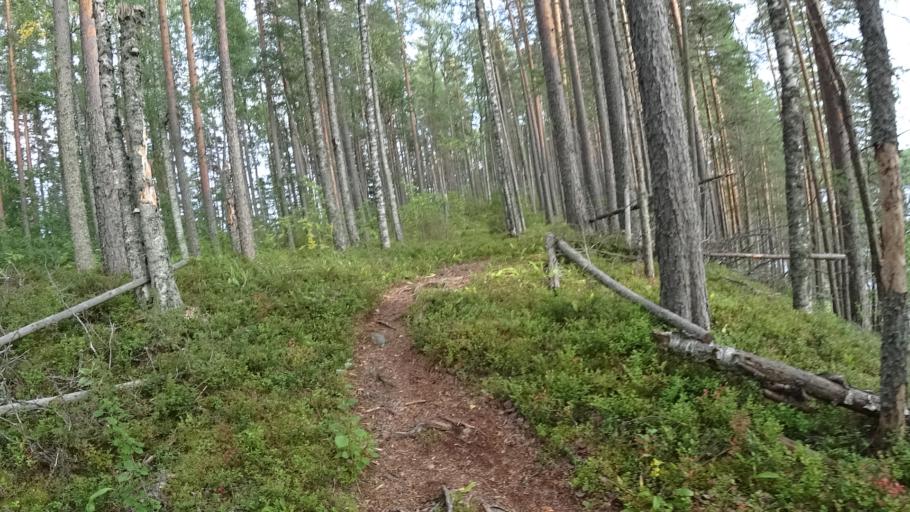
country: FI
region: North Karelia
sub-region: Joensuu
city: Ilomantsi
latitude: 62.5725
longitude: 31.1754
